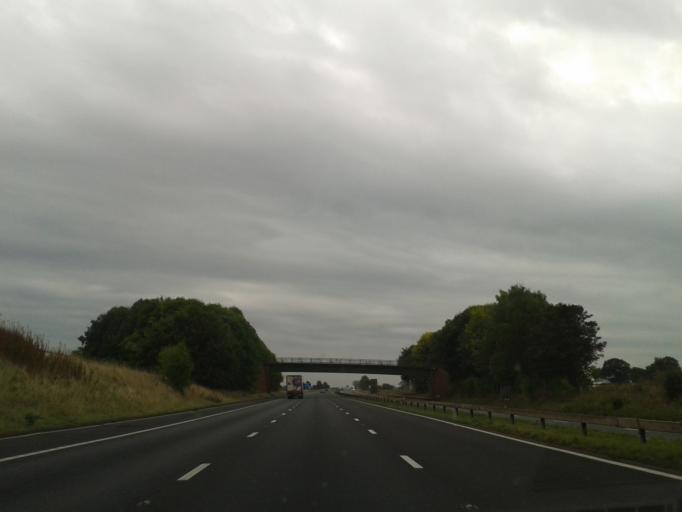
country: GB
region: England
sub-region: Cumbria
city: Penrith
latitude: 54.7163
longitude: -2.7972
